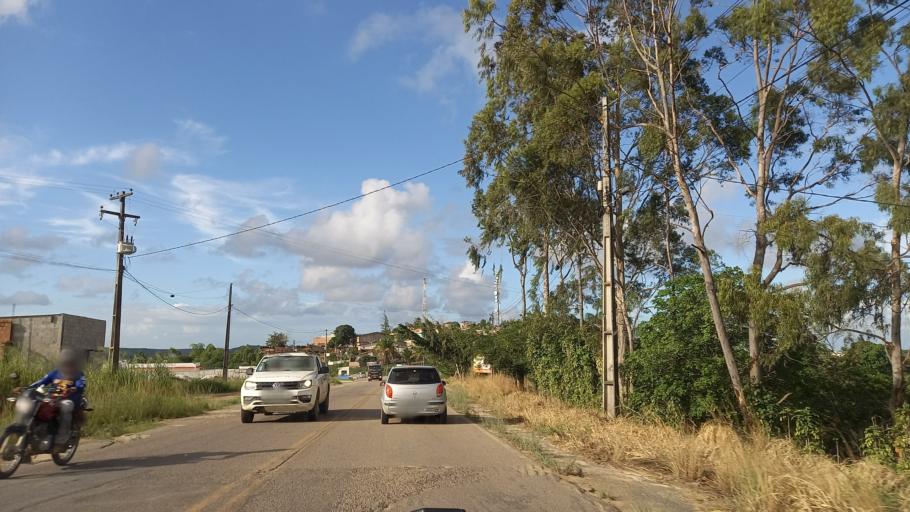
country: BR
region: Pernambuco
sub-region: Rio Formoso
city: Rio Formoso
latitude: -8.6733
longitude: -35.1588
